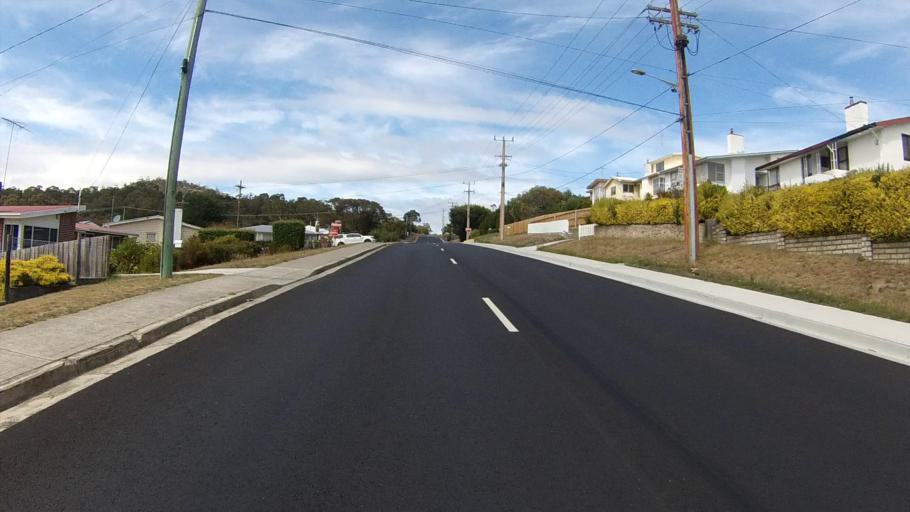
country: AU
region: Tasmania
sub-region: Clarence
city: Lindisfarne
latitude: -42.8136
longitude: 147.3513
